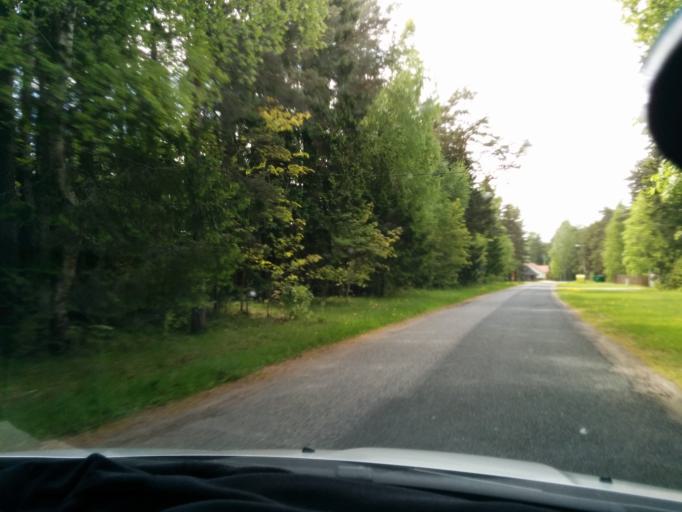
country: EE
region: Harju
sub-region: Loksa linn
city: Loksa
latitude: 59.5618
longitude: 25.6733
